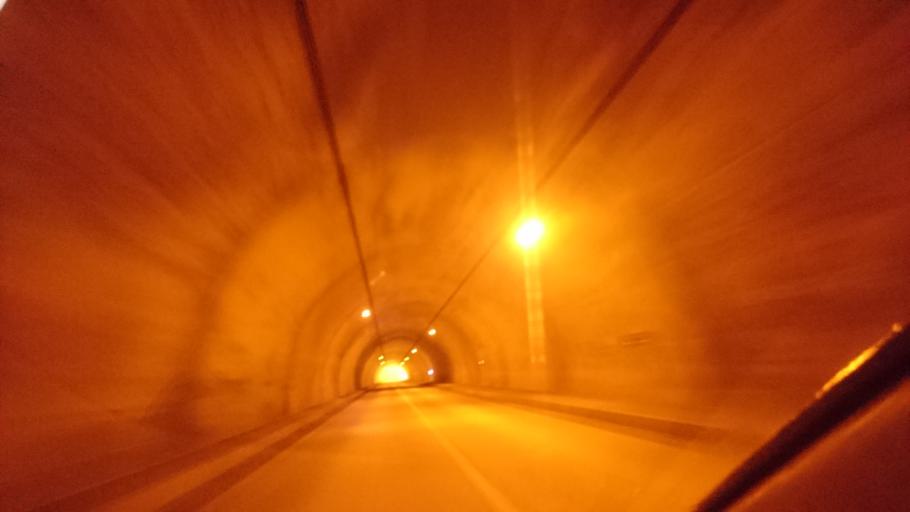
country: JP
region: Iwate
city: Mizusawa
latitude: 39.1222
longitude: 140.9063
